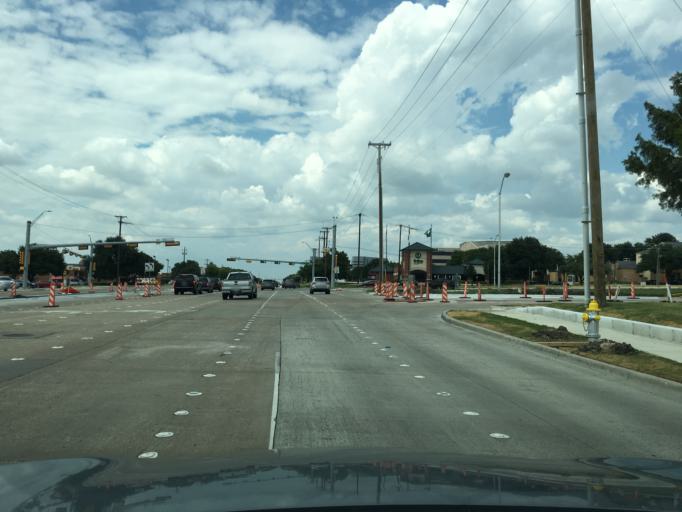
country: US
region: Texas
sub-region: Dallas County
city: Addison
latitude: 33.0157
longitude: -96.7952
